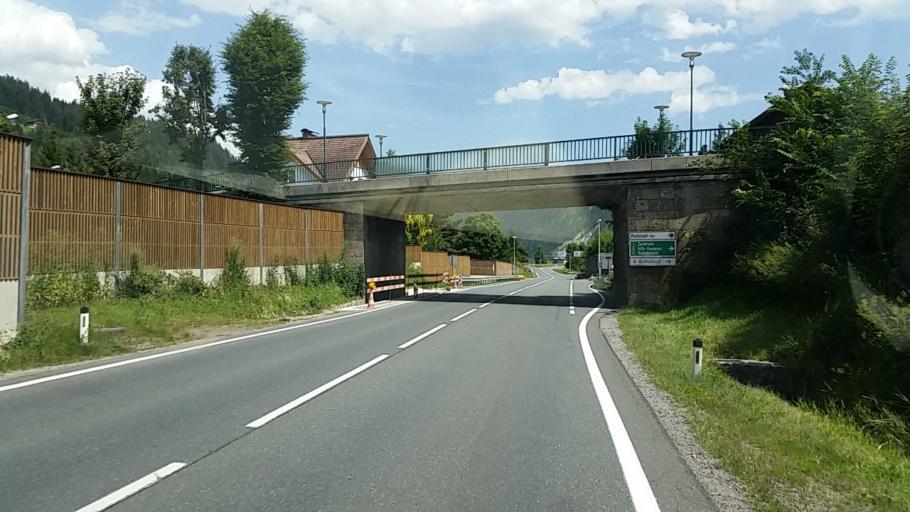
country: AT
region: Salzburg
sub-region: Politischer Bezirk Sankt Johann im Pongau
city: Radstadt
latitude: 47.3860
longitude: 13.4670
